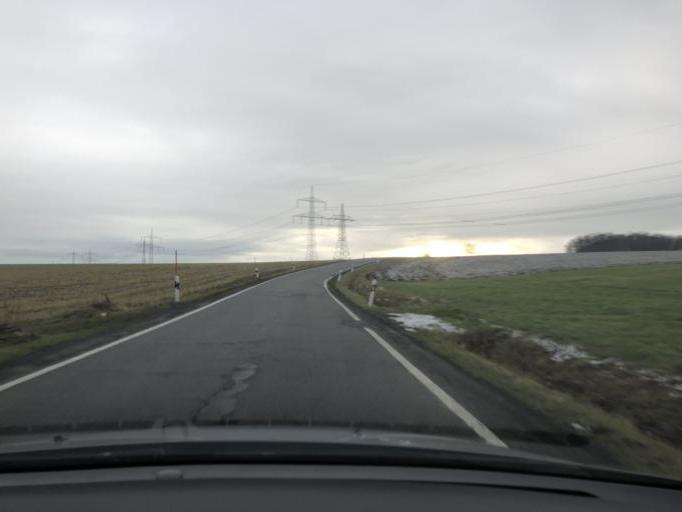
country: DE
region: Saxony
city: Niederfrohna
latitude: 50.8788
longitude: 12.7201
